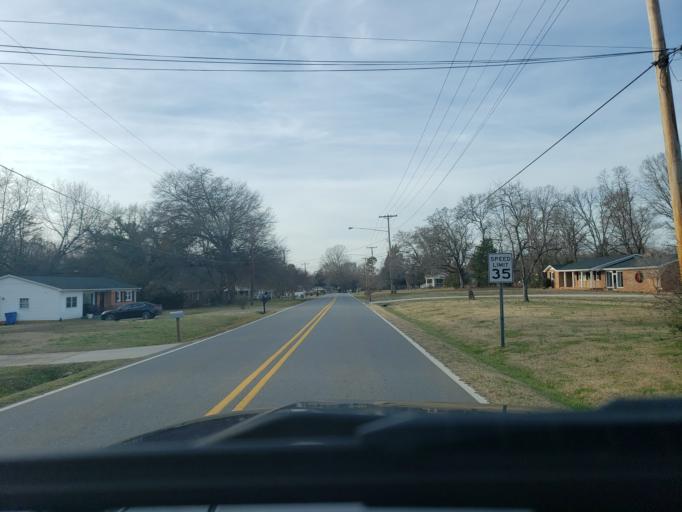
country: US
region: North Carolina
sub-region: Cleveland County
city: Shelby
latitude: 35.2755
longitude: -81.5046
